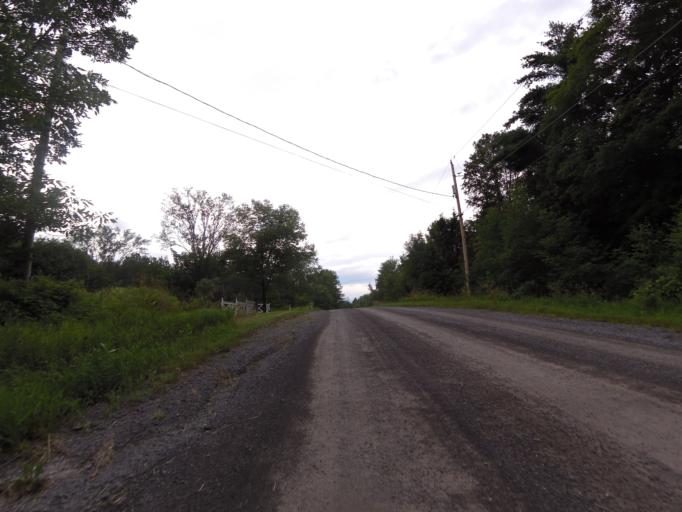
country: CA
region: Ontario
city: Carleton Place
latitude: 45.1516
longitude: -76.2578
